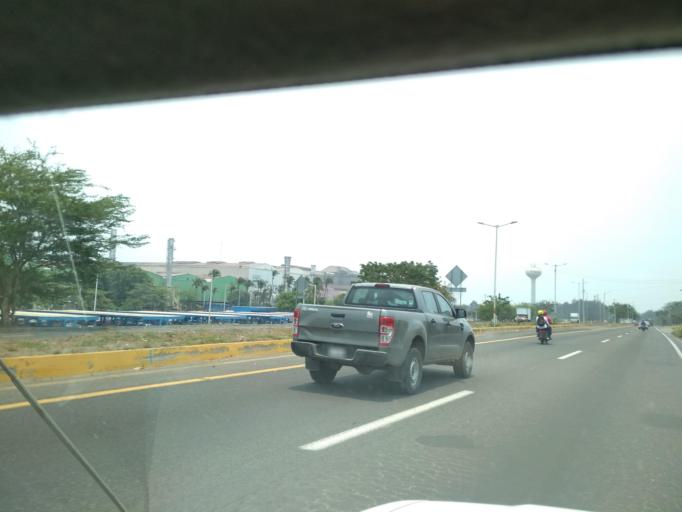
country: MX
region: Veracruz
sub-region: Veracruz
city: Oasis
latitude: 19.1781
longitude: -96.2469
